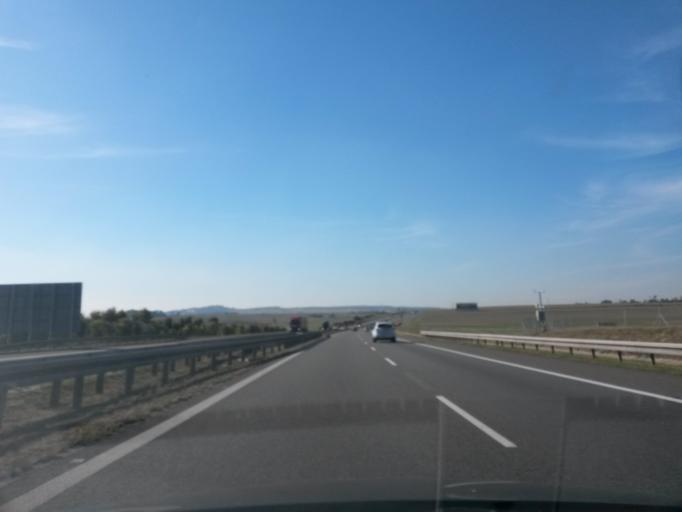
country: PL
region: Opole Voivodeship
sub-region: Powiat strzelecki
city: Lesnica
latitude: 50.4591
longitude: 18.2420
